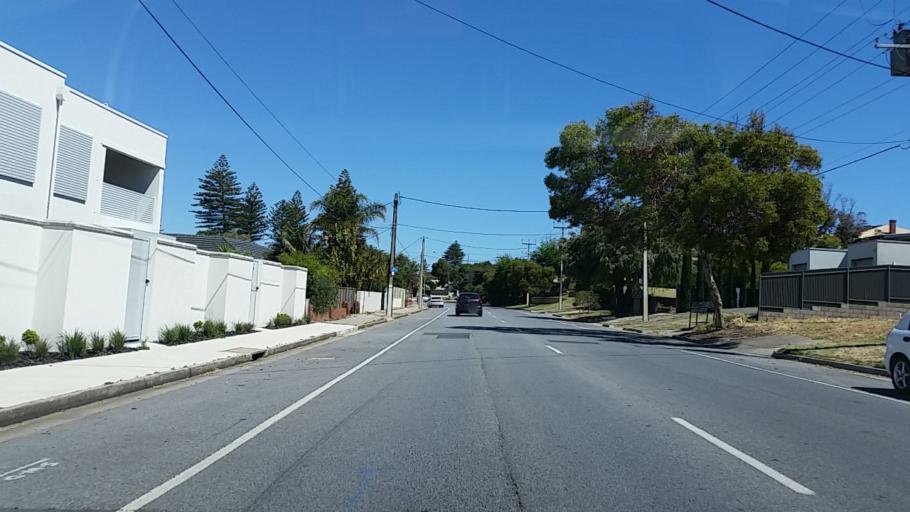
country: AU
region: South Australia
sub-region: Charles Sturt
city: Grange
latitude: -34.9091
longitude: 138.4924
